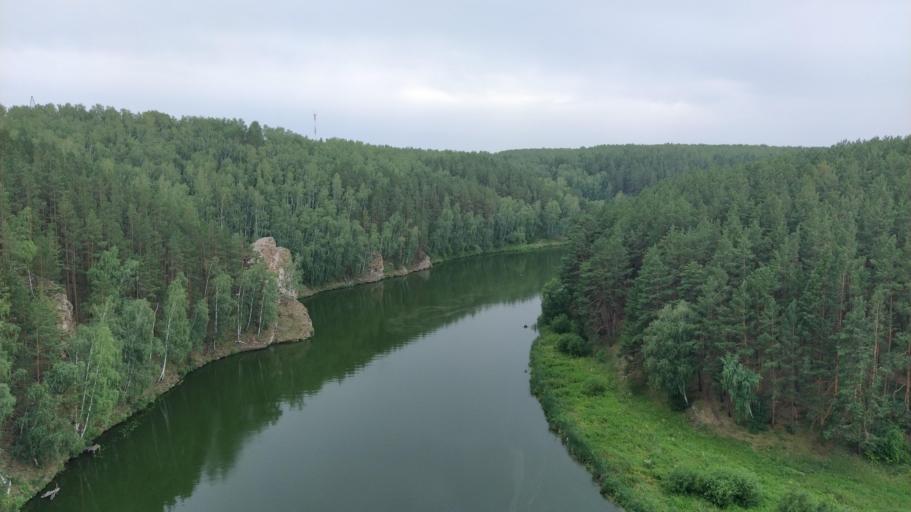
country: RU
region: Sverdlovsk
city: Martyush
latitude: 56.4070
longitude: 61.8748
